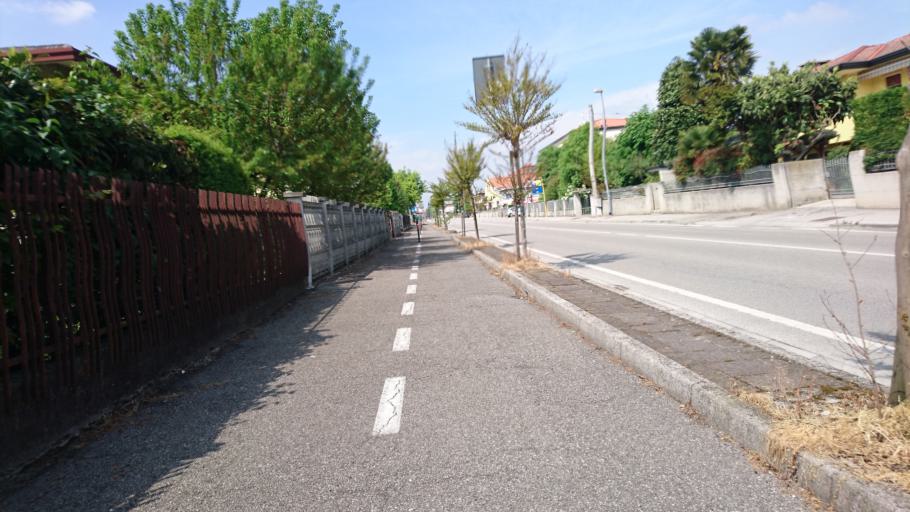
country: IT
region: Veneto
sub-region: Provincia di Padova
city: Saletto
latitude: 45.4743
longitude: 11.8605
